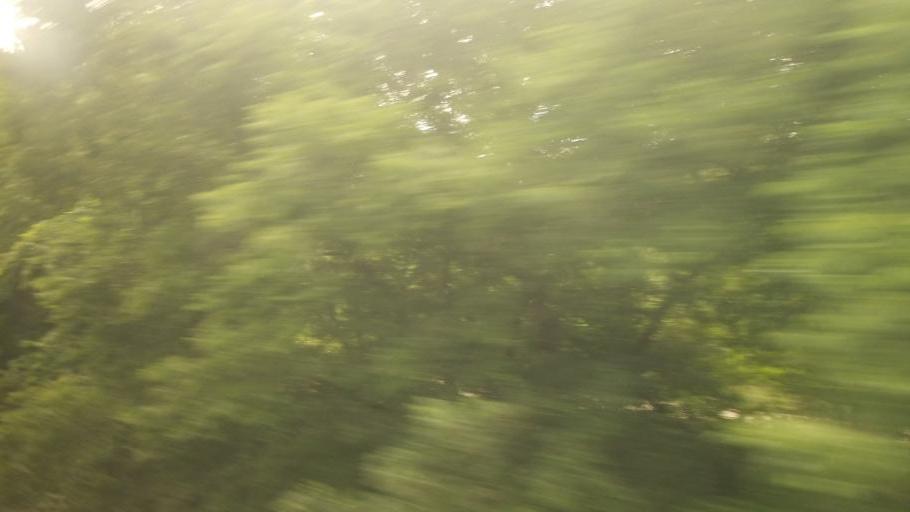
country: US
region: Kansas
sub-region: Shawnee County
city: Topeka
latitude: 39.0353
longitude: -95.6713
